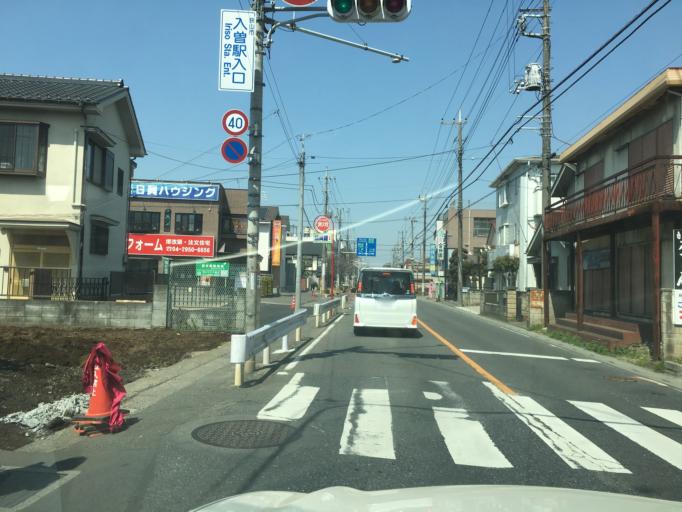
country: JP
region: Saitama
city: Sayama
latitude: 35.8340
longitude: 139.4289
